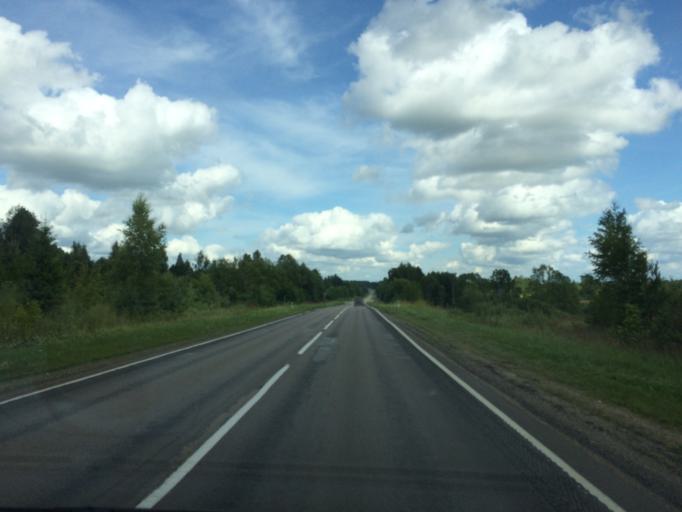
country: LV
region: Rezekne
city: Rezekne
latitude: 56.5998
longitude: 27.4239
